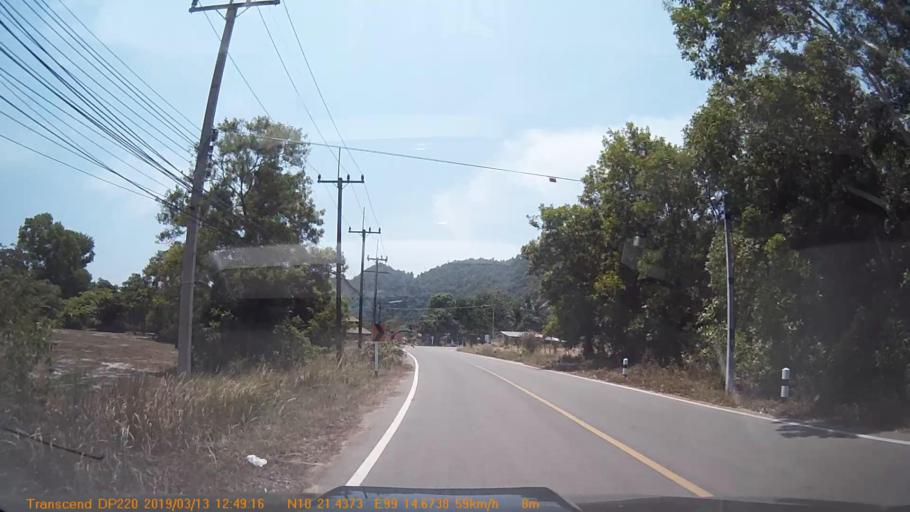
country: TH
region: Chumphon
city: Chumphon
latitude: 10.3570
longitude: 99.2443
